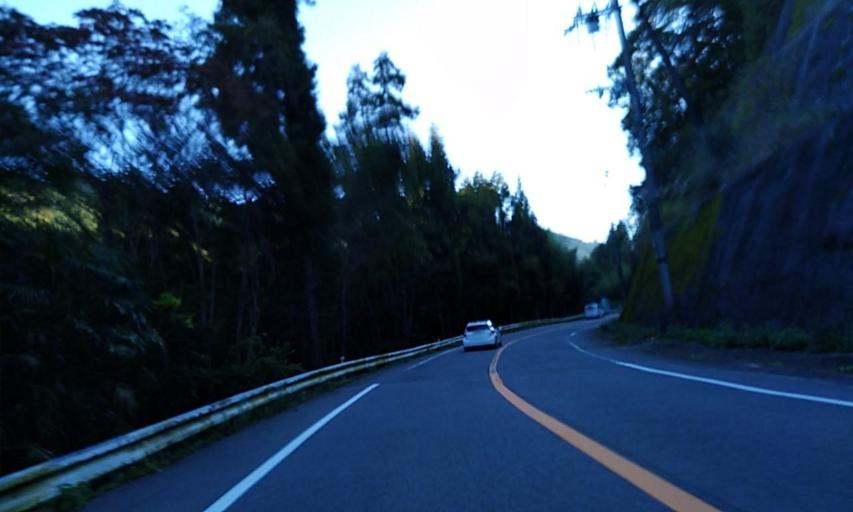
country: JP
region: Wakayama
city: Iwade
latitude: 34.1560
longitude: 135.3206
